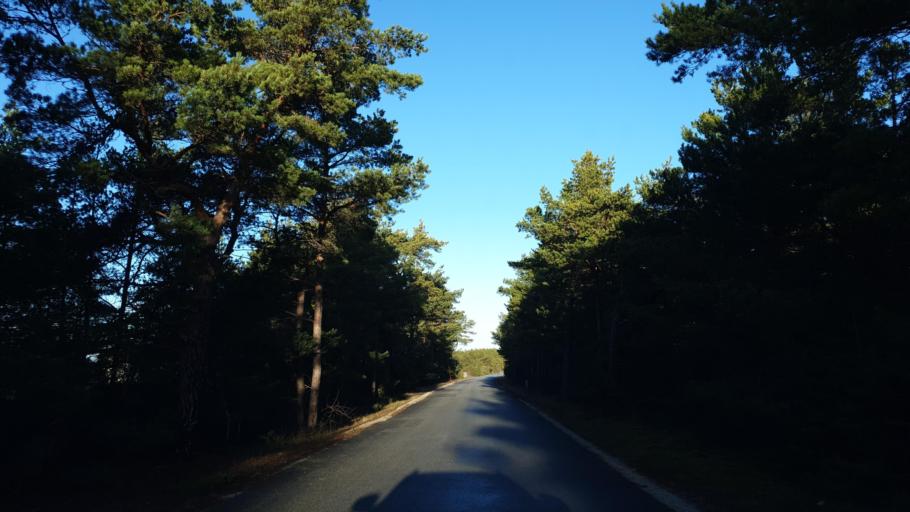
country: SE
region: Gotland
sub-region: Gotland
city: Slite
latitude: 57.9756
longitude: 19.1533
